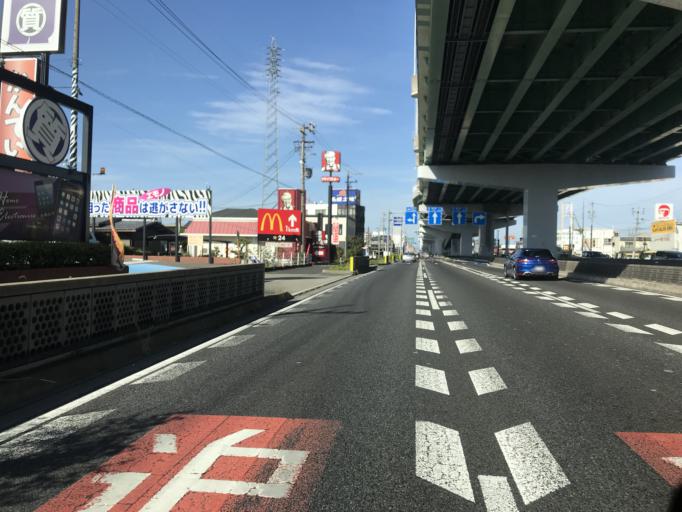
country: JP
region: Aichi
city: Iwakura
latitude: 35.2457
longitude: 136.8451
